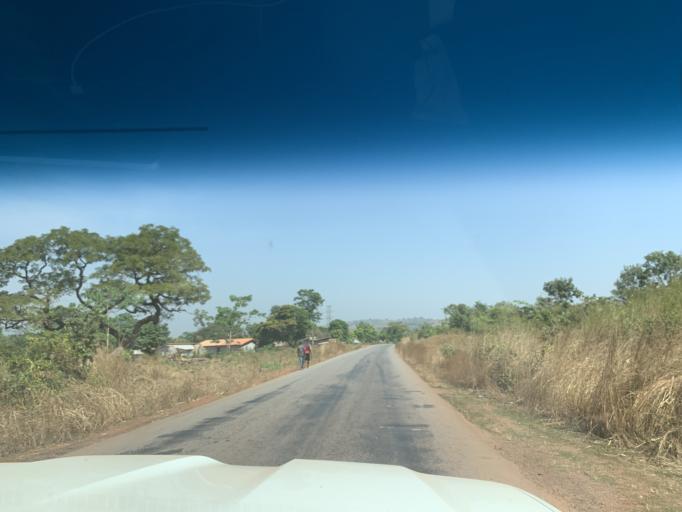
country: GN
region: Kindia
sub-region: Kindia
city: Kindia
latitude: 10.0340
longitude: -12.6686
